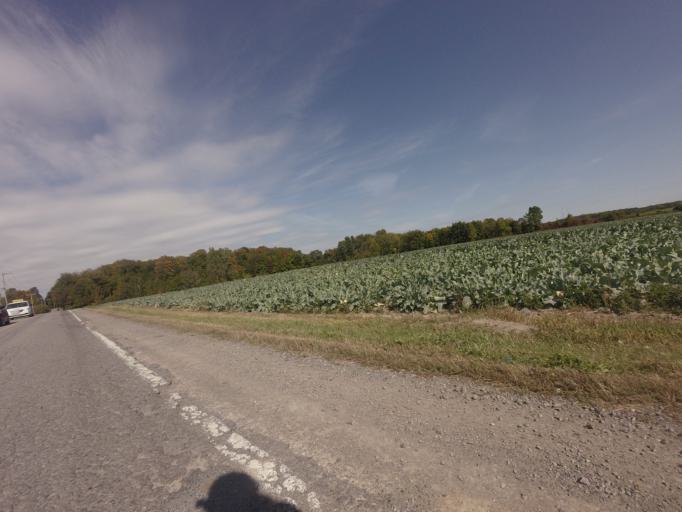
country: CA
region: Quebec
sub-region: Laurentides
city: Saint-Eustache
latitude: 45.6015
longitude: -73.9164
